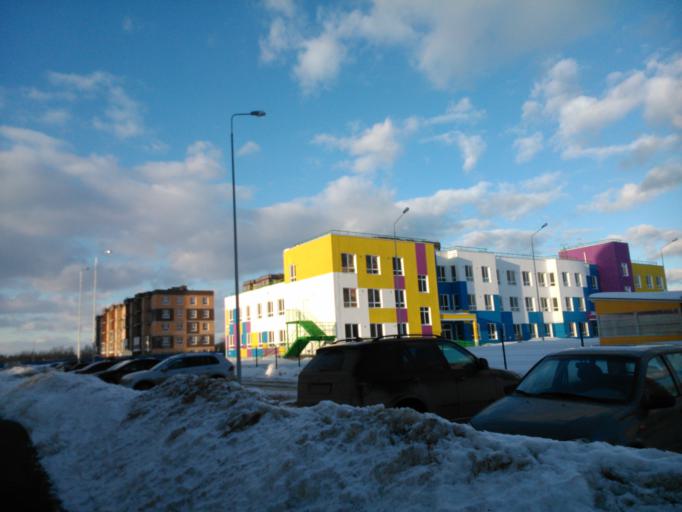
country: RU
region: Perm
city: Perm
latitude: 58.0032
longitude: 56.3369
